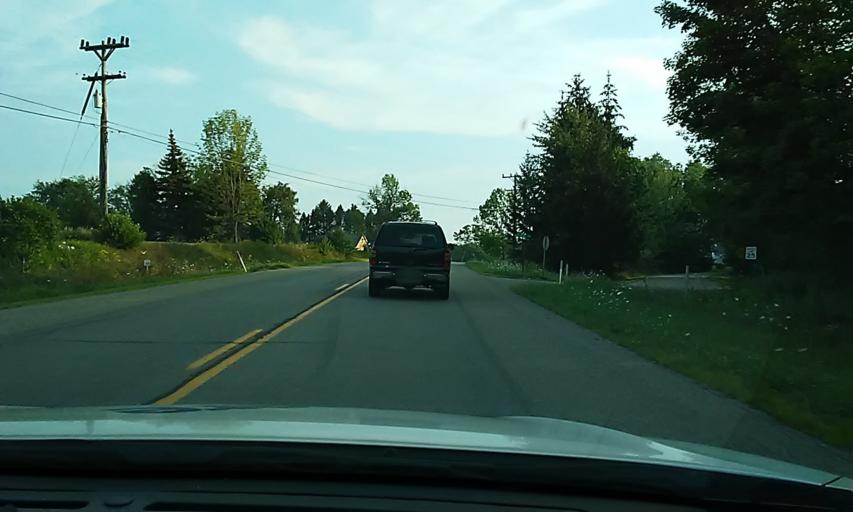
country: US
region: Pennsylvania
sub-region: McKean County
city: Kane
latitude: 41.6800
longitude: -78.7242
